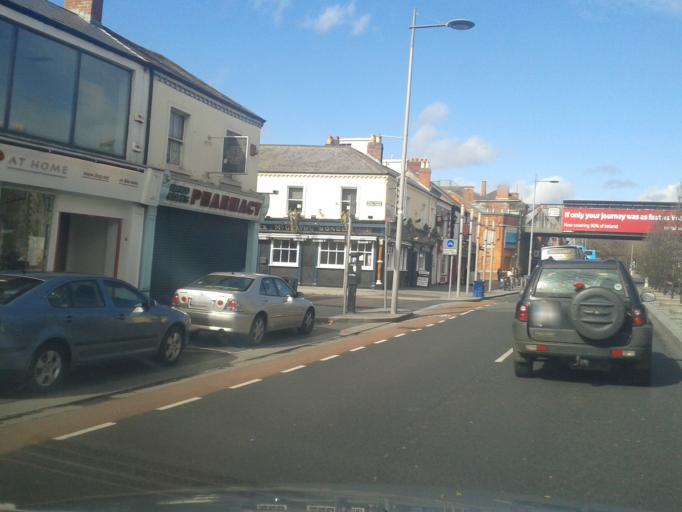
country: IE
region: Leinster
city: Drumcondra
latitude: 53.3623
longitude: -6.2590
